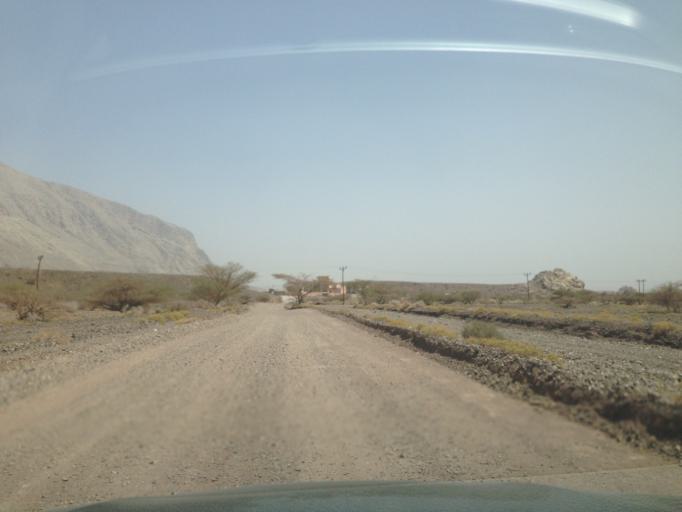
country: OM
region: Az Zahirah
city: `Ibri
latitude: 23.1764
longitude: 56.9012
